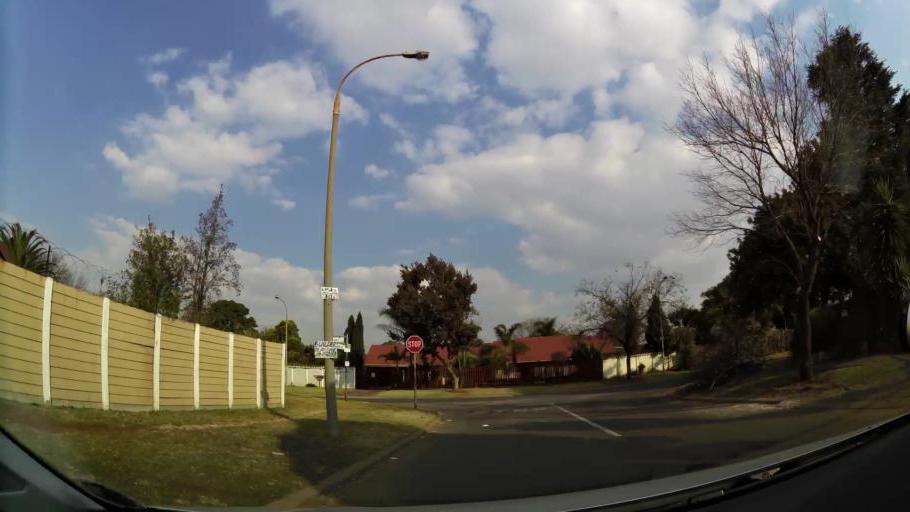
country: ZA
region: Gauteng
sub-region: City of Johannesburg Metropolitan Municipality
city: Modderfontein
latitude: -26.0972
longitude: 28.1985
